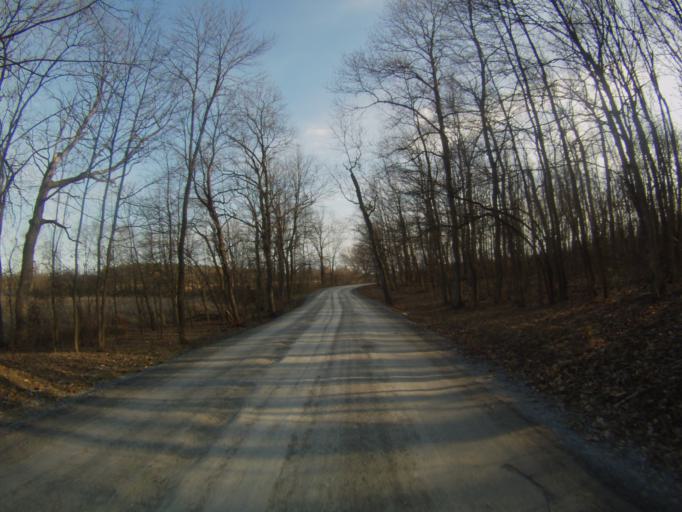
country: US
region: New York
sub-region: Essex County
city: Port Henry
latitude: 44.0766
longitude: -73.3501
